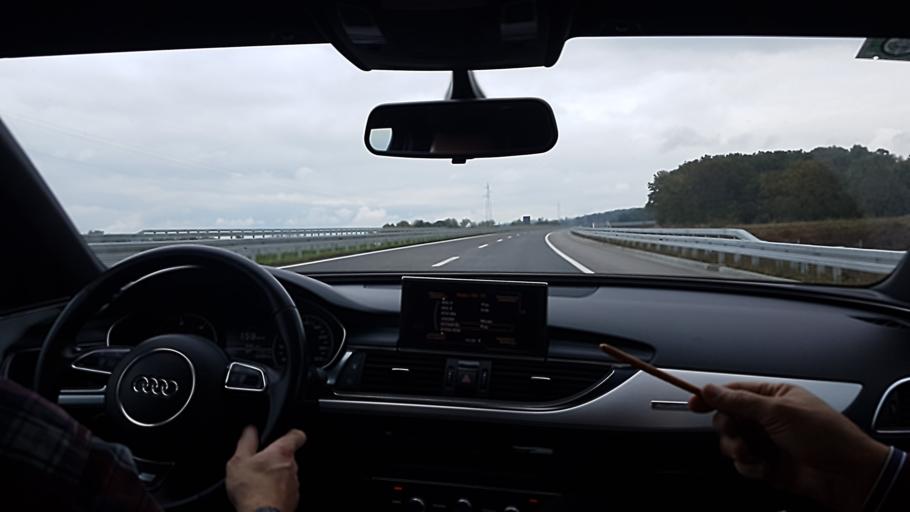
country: BA
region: Republika Srpska
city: Prnjavor
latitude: 44.8551
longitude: 17.6962
